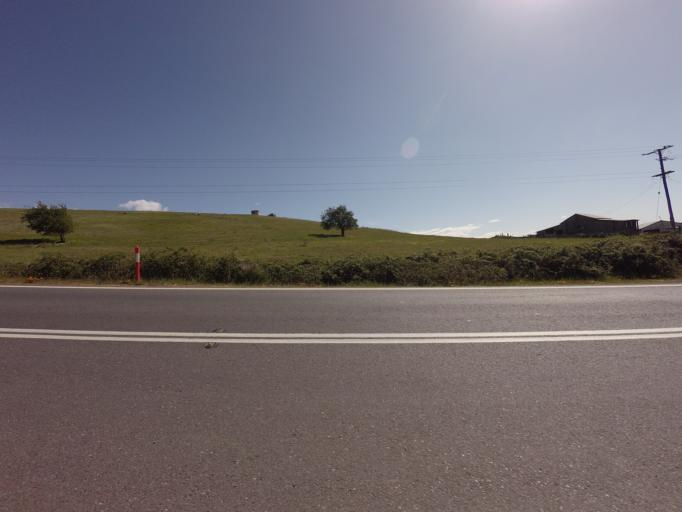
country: AU
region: Tasmania
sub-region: Derwent Valley
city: New Norfolk
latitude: -42.6954
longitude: 146.9387
